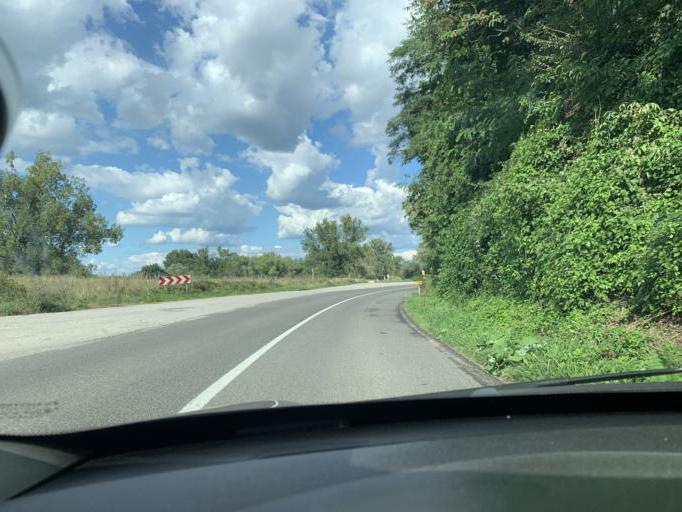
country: SK
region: Trenciansky
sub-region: Okres Trencin
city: Trencin
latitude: 48.8277
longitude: 17.9437
